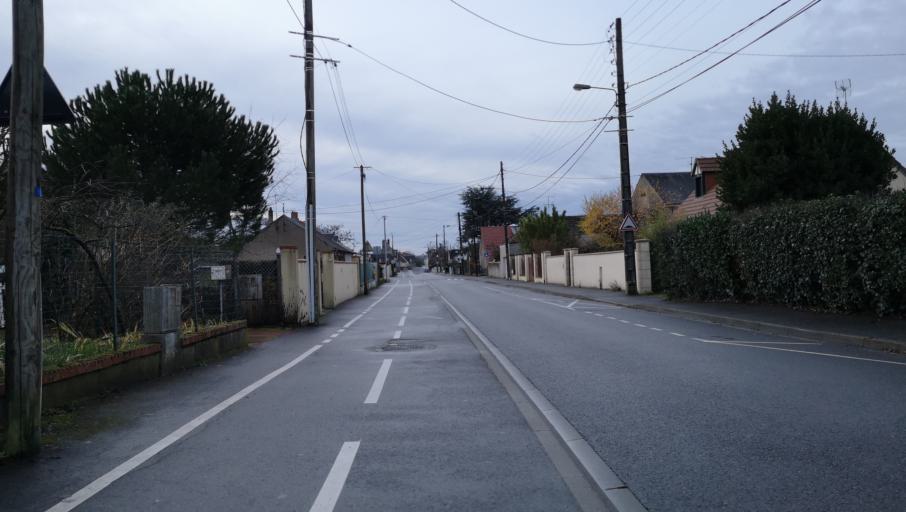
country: FR
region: Centre
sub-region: Departement du Loiret
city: Saint-Jean-de-Braye
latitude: 47.9204
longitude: 1.9649
